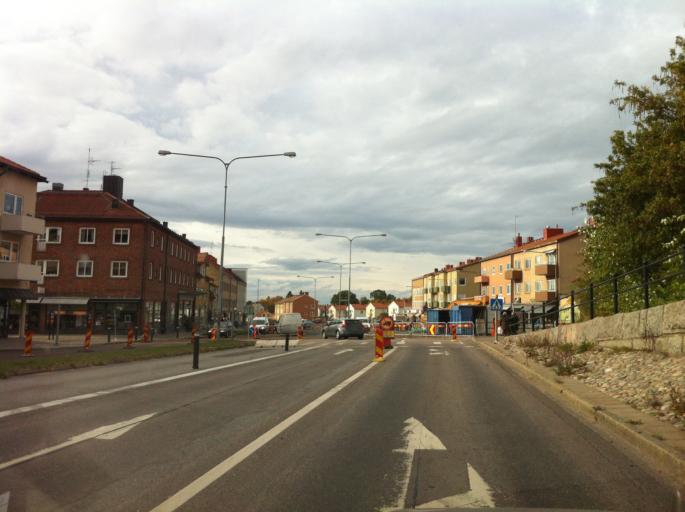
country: SE
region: OEstergoetland
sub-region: Motala Kommun
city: Motala
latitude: 58.5372
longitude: 15.0414
